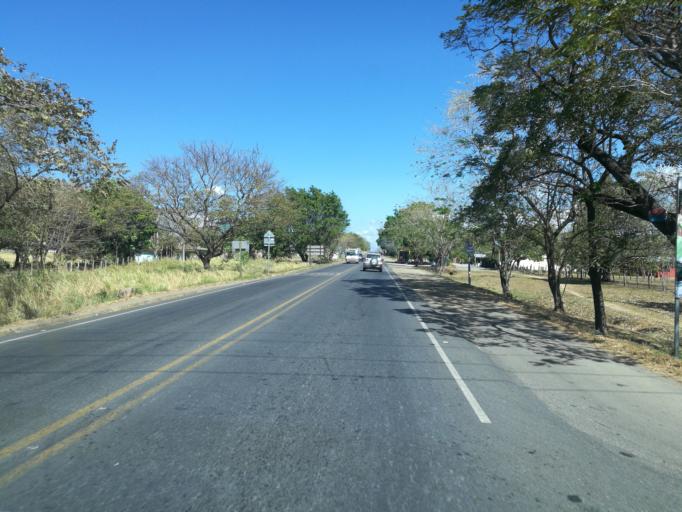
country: CR
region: Guanacaste
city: Liberia
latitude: 10.6598
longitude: -85.4697
